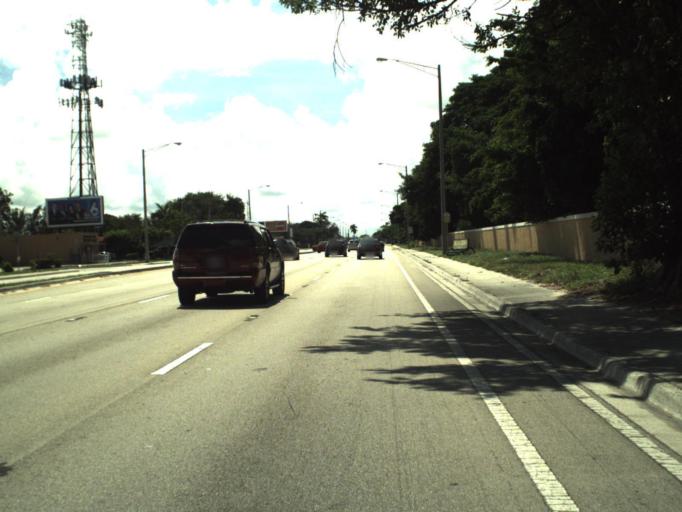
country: US
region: Florida
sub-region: Broward County
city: Carver Ranches
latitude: 25.9956
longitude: -80.1865
